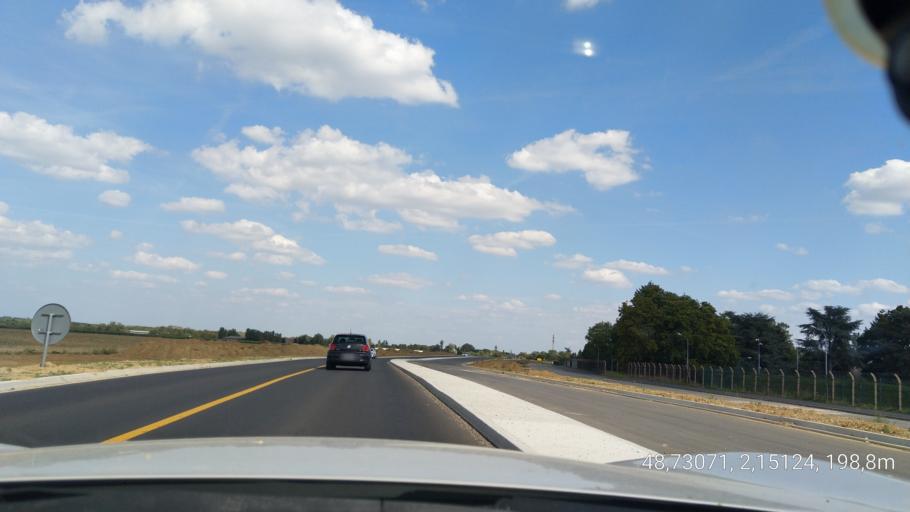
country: FR
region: Ile-de-France
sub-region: Departement de l'Essonne
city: Saclay
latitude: 48.7309
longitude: 2.1510
